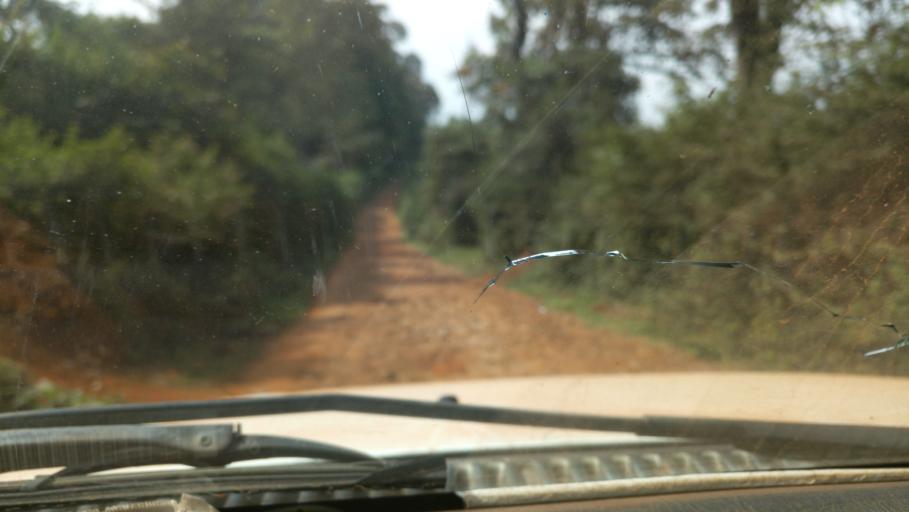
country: KE
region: Murang'a District
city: Kangema
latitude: -0.7199
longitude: 37.0318
